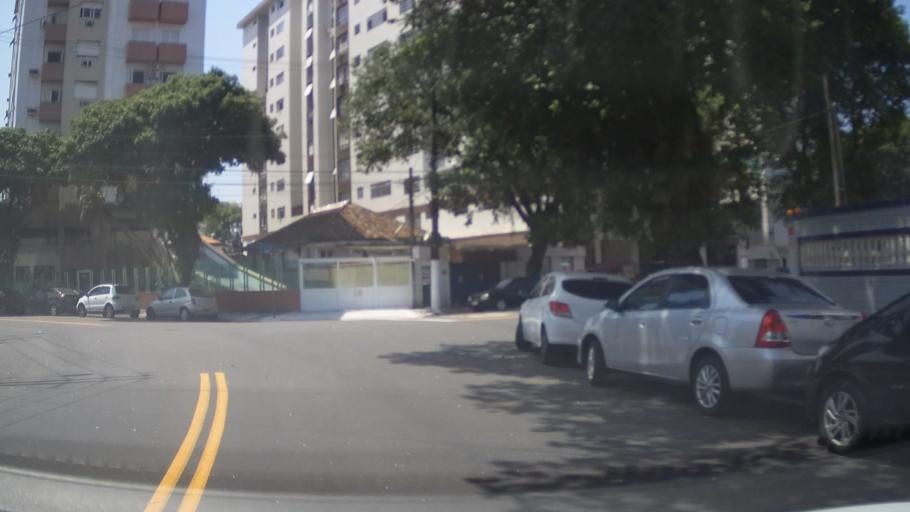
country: BR
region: Sao Paulo
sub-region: Santos
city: Santos
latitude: -23.9728
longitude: -46.3037
